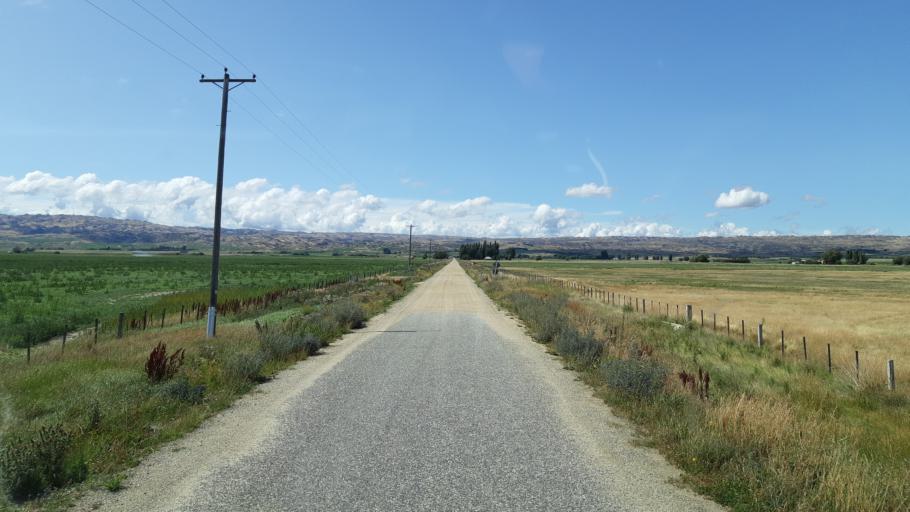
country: NZ
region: Otago
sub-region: Queenstown-Lakes District
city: Wanaka
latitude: -45.2038
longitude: 169.6515
